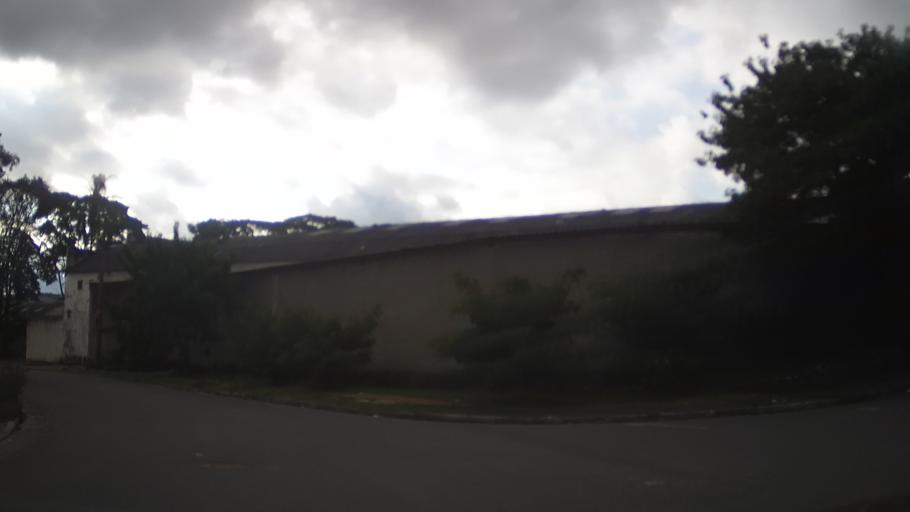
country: BR
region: Sao Paulo
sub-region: Guarulhos
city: Guarulhos
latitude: -23.4612
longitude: -46.4799
